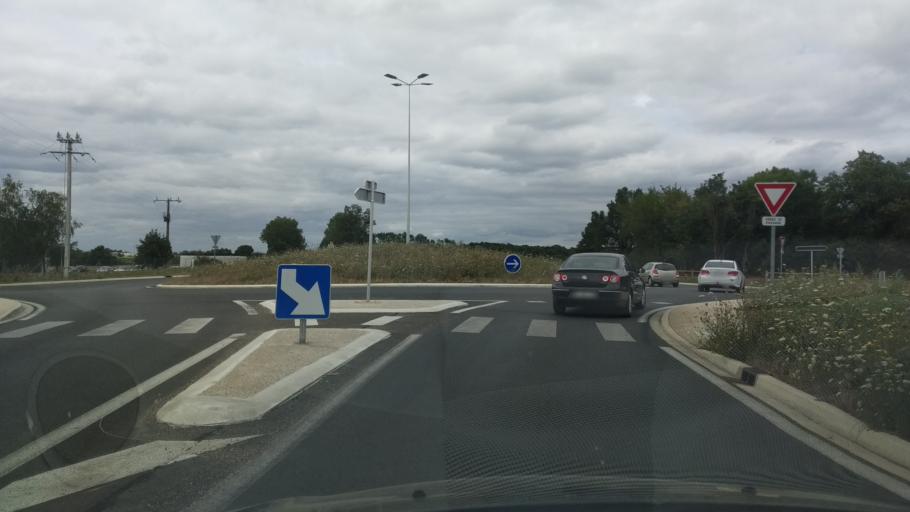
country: FR
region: Poitou-Charentes
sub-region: Departement de la Vienne
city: Roches-Premarie-Andille
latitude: 46.4943
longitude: 0.3662
